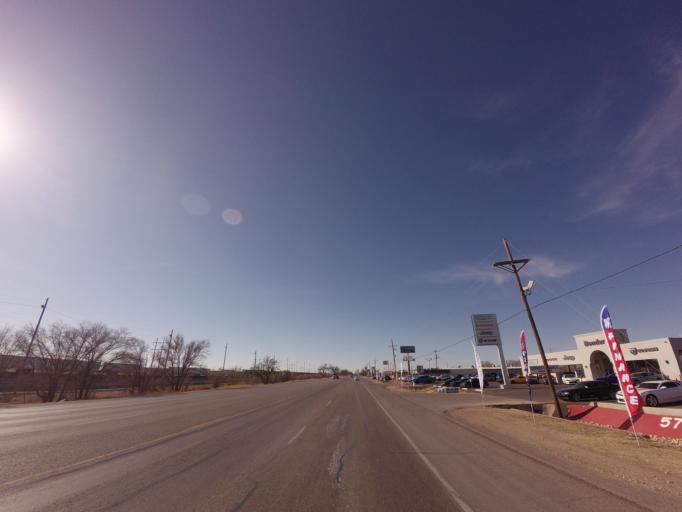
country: US
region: New Mexico
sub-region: Curry County
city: Clovis
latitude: 34.3953
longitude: -103.1611
